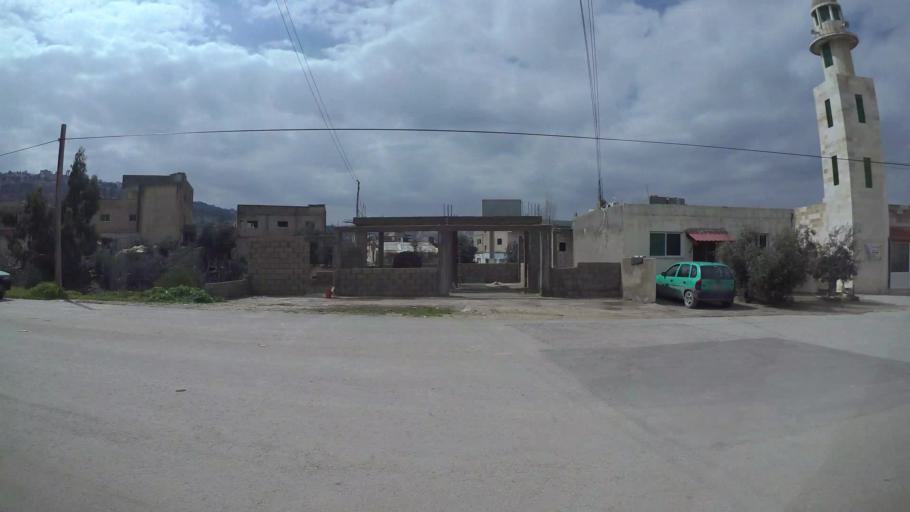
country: JO
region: Amman
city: Al Jubayhah
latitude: 32.0509
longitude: 35.8234
